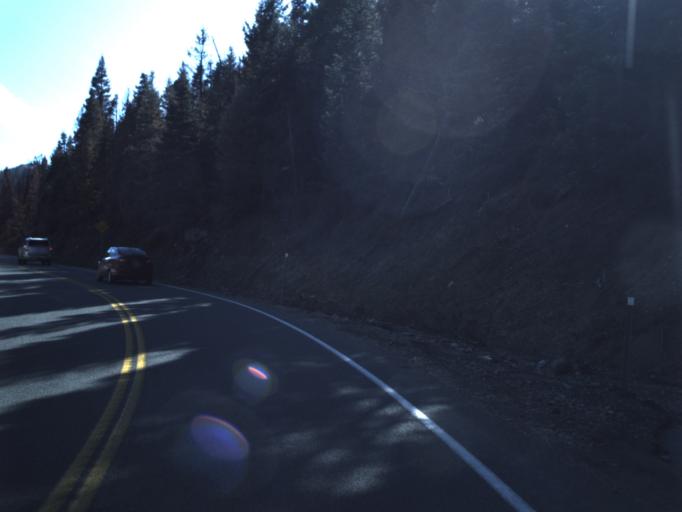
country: US
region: Utah
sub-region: Iron County
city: Parowan
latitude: 37.7324
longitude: -112.8383
